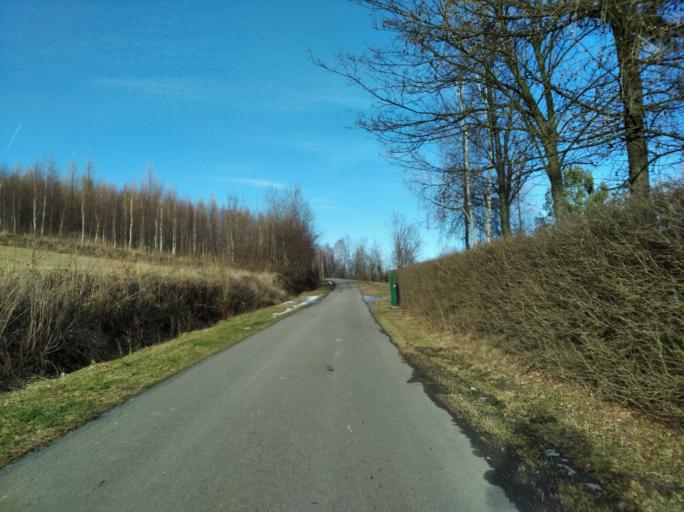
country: PL
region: Subcarpathian Voivodeship
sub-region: Powiat strzyzowski
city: Gwoznica Gorna
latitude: 49.8178
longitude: 21.9900
